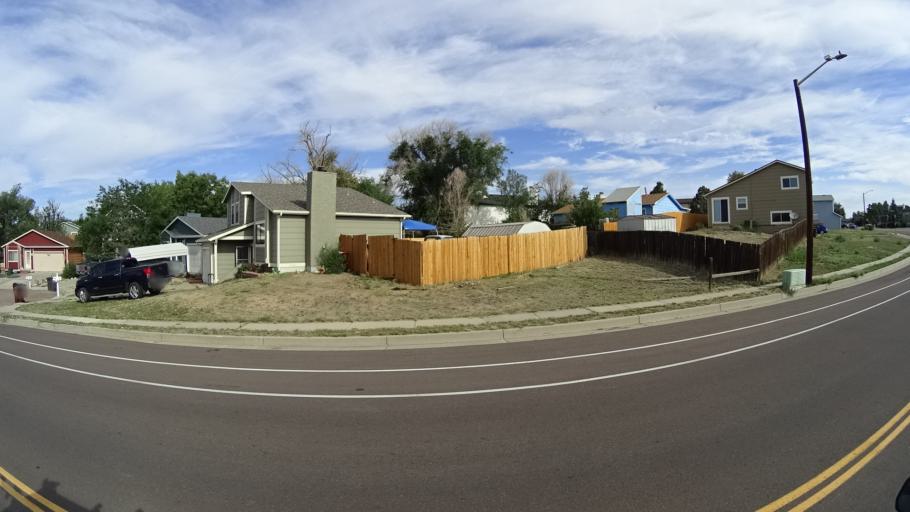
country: US
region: Colorado
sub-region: El Paso County
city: Fountain
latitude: 38.6874
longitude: -104.6936
